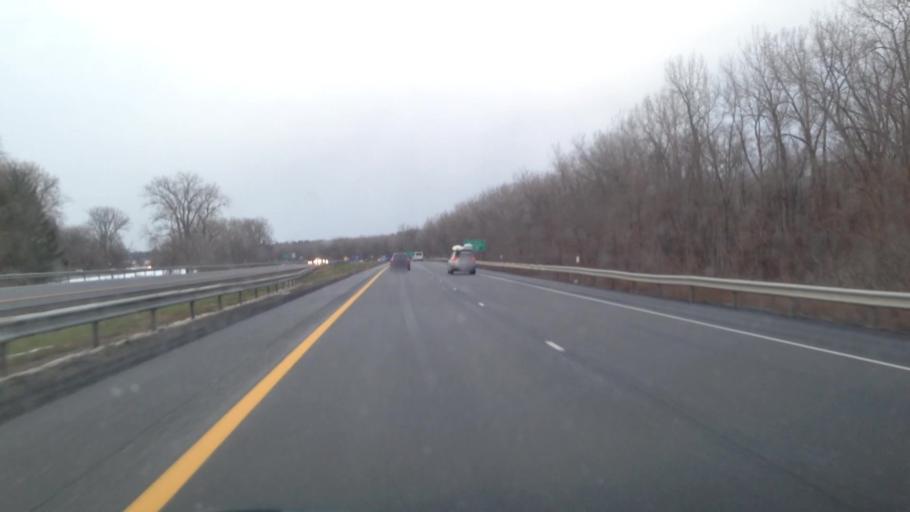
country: US
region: New York
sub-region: Montgomery County
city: Canajoharie
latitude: 42.8997
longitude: -74.5434
